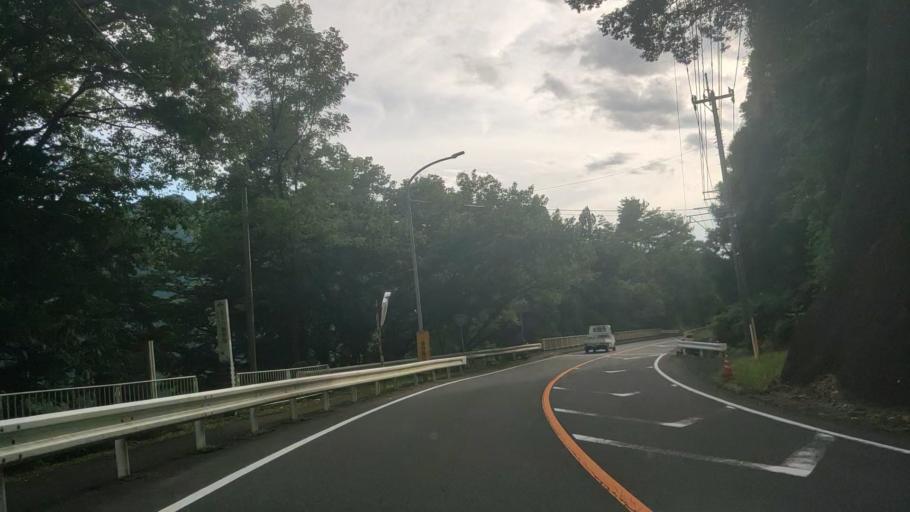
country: JP
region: Gunma
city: Omamacho-omama
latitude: 36.5412
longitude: 139.3690
